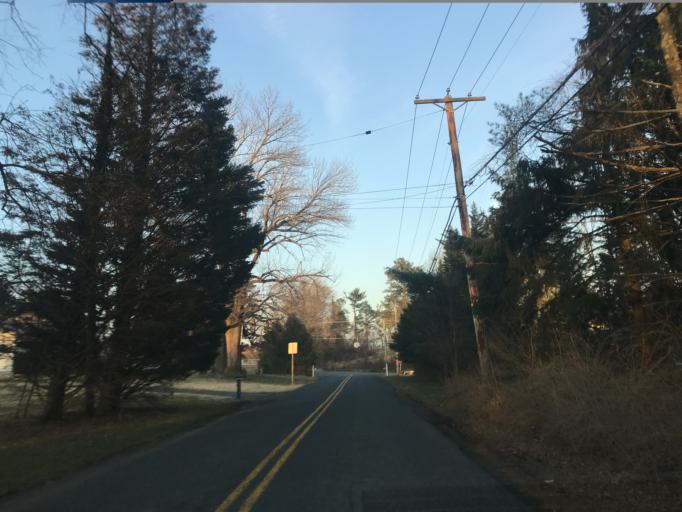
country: US
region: Maryland
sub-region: Harford County
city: Riverside
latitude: 39.4944
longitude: -76.2627
